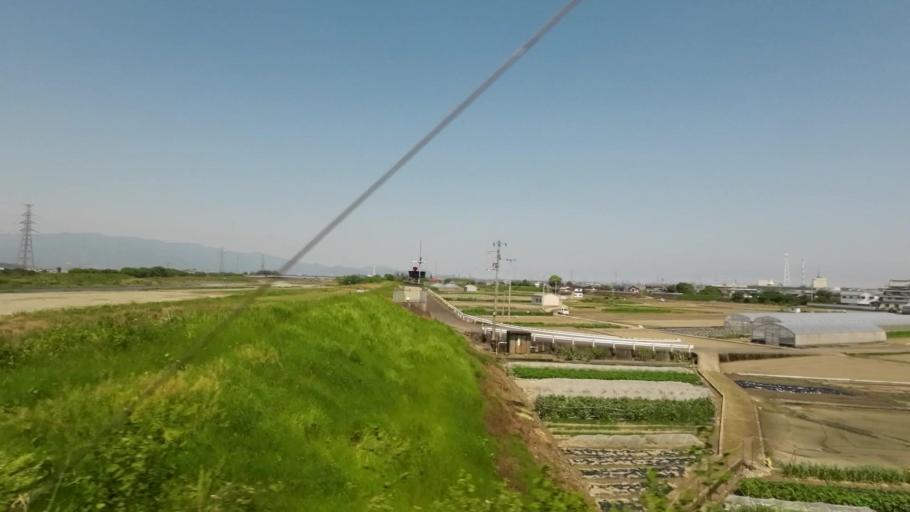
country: JP
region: Ehime
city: Saijo
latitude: 33.9069
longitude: 133.1805
